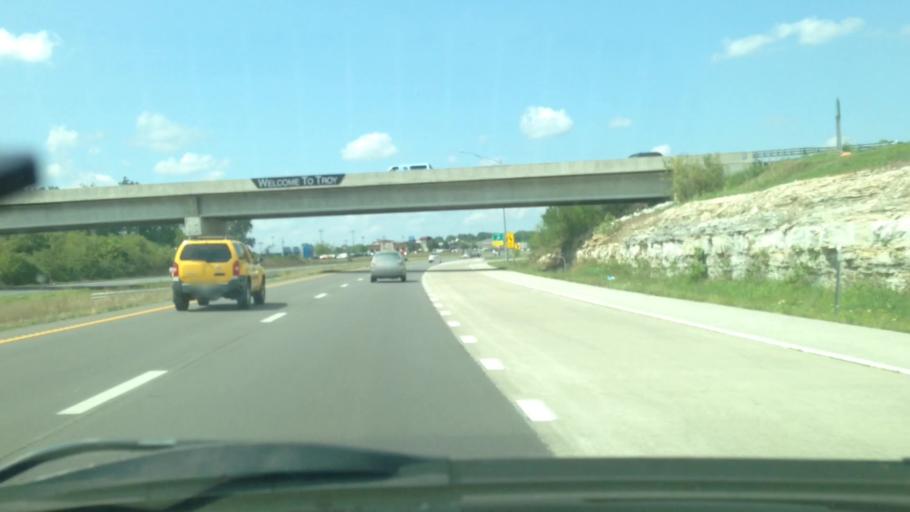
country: US
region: Missouri
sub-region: Lincoln County
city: Troy
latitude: 38.9665
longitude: -90.9561
